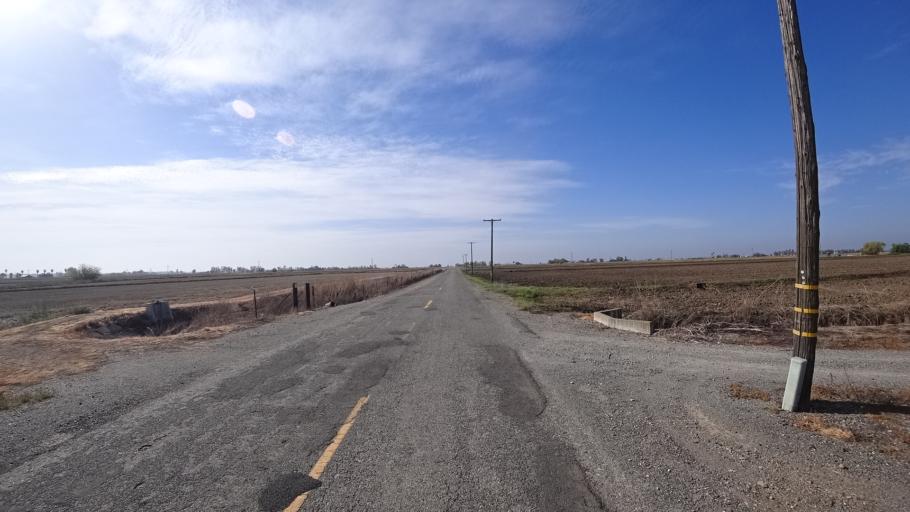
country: US
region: California
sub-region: Glenn County
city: Hamilton City
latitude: 39.5966
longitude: -122.0464
